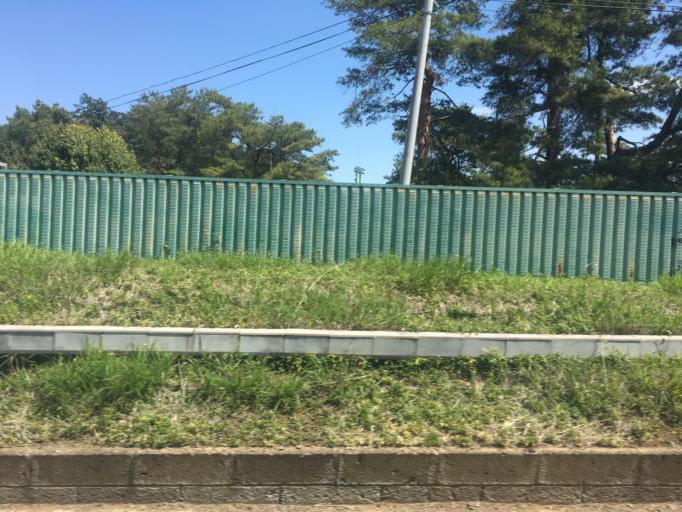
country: JP
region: Saitama
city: Sakado
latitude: 35.9330
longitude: 139.4304
